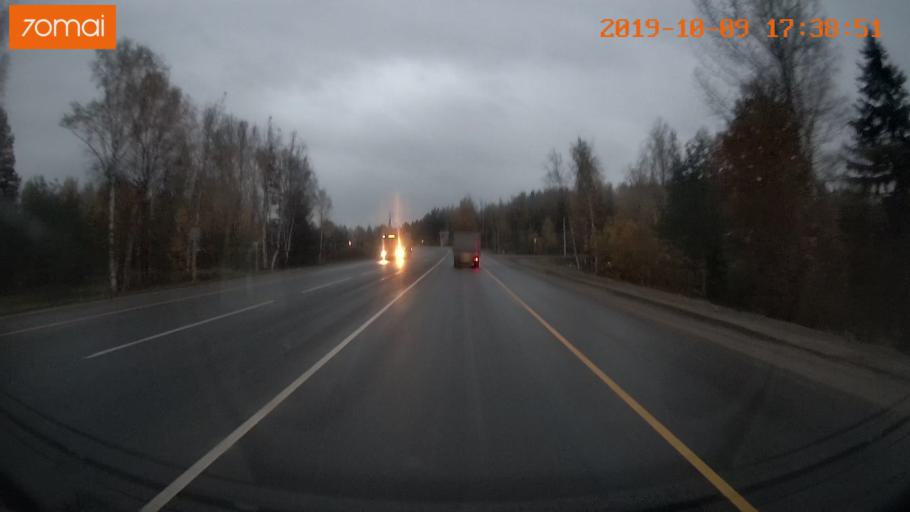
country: RU
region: Ivanovo
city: Bogorodskoye
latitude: 57.0665
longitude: 40.9524
